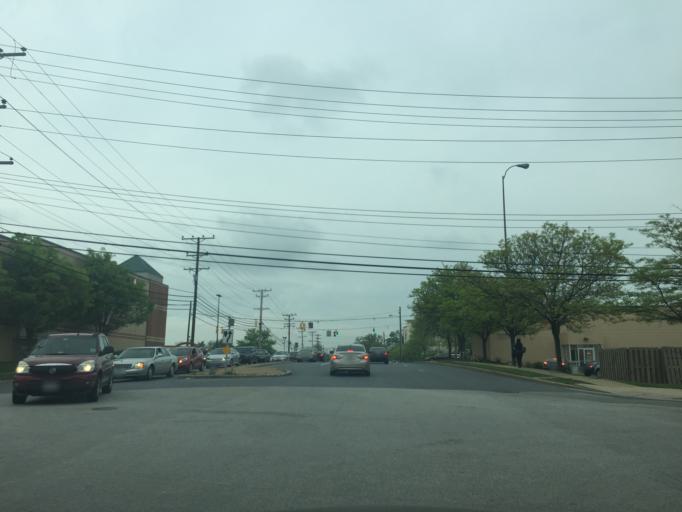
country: US
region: Maryland
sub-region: Baltimore County
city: Catonsville
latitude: 39.2902
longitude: -76.7316
